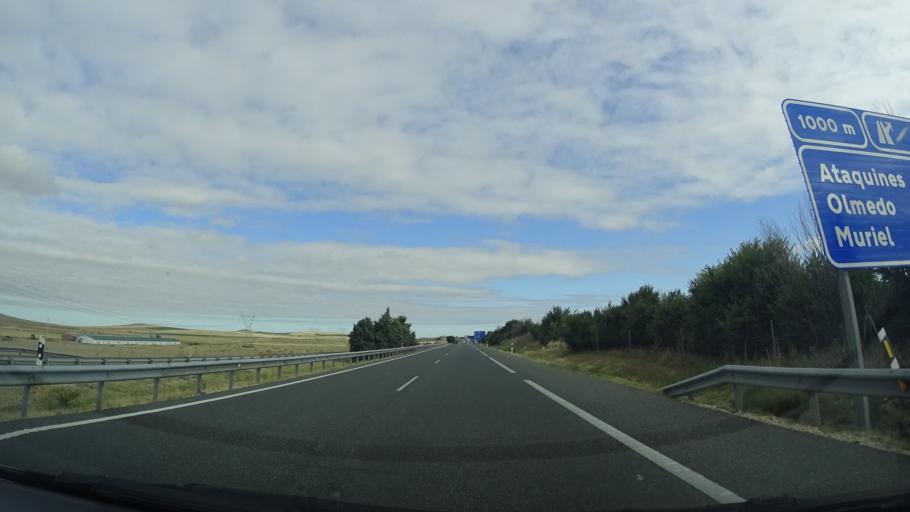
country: ES
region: Castille and Leon
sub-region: Provincia de Valladolid
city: Ataquines
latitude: 41.1652
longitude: -4.7993
